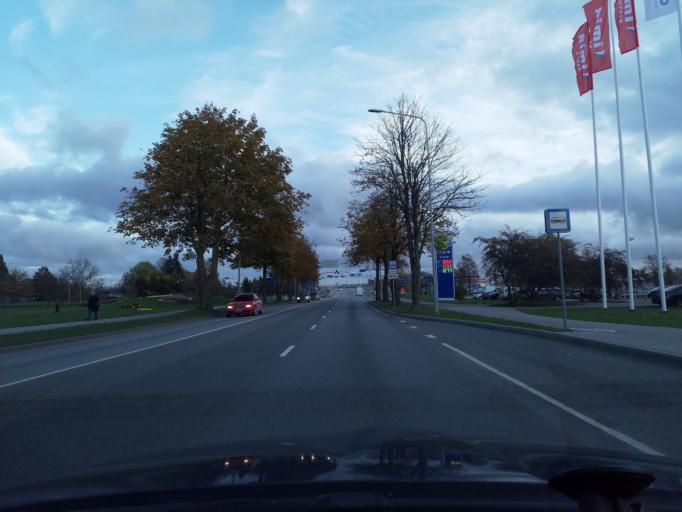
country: LV
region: Ventspils
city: Ventspils
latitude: 57.3884
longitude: 21.5802
